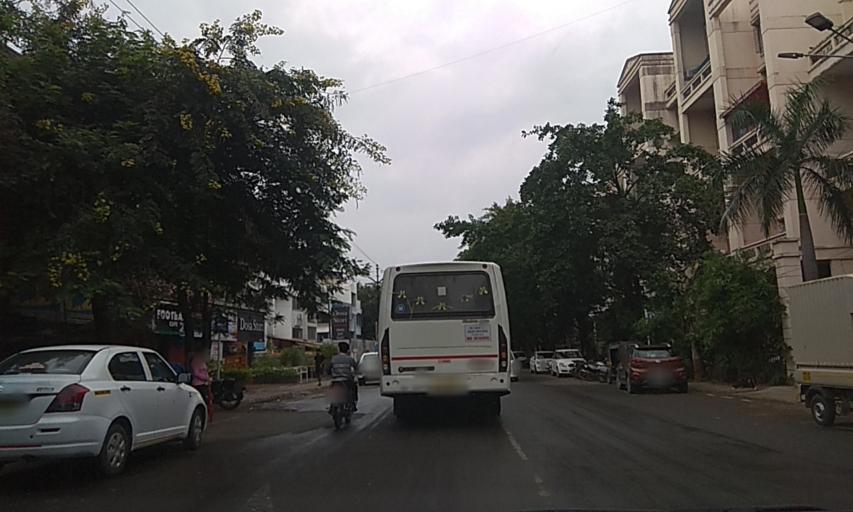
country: IN
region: Maharashtra
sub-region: Pune Division
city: Lohogaon
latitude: 18.5652
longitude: 73.9127
